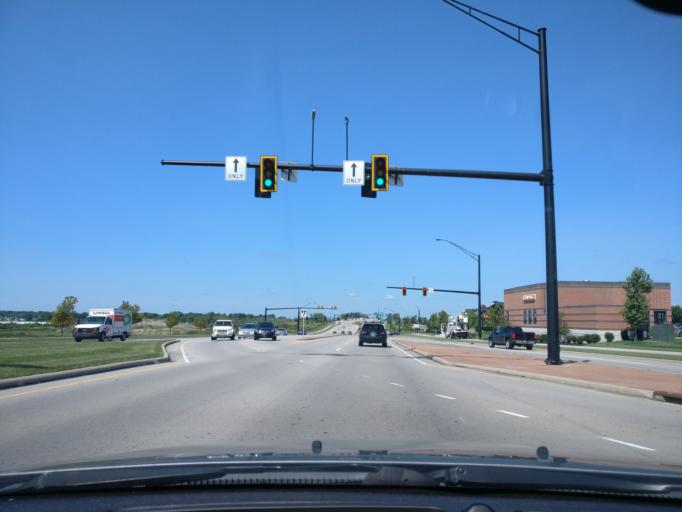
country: US
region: Ohio
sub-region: Warren County
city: Springboro
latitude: 39.5968
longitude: -84.2307
